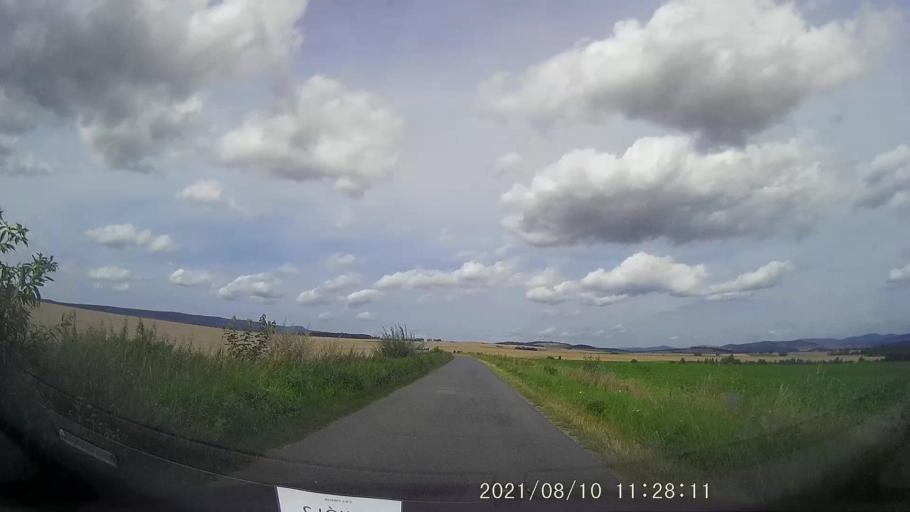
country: PL
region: Lower Silesian Voivodeship
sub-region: Powiat klodzki
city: Polanica-Zdroj
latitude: 50.4383
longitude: 16.5789
